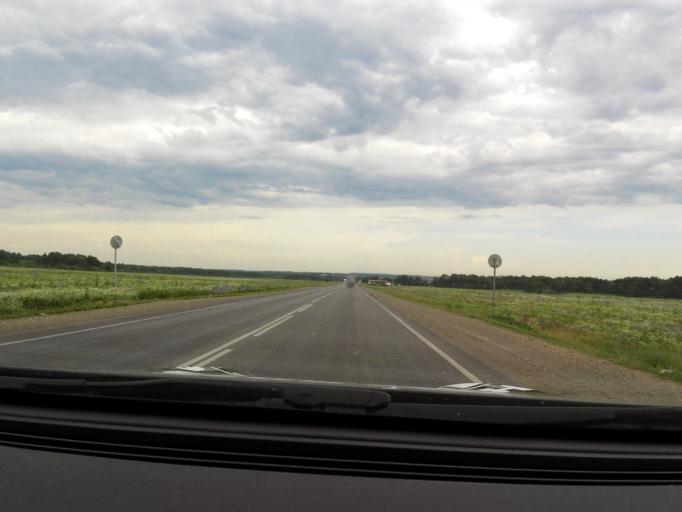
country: RU
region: Bashkortostan
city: Kudeyevskiy
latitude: 54.8173
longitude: 56.8155
